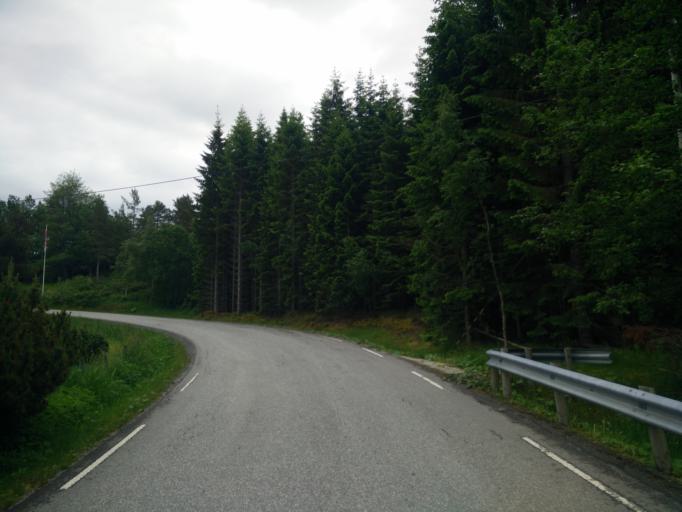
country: NO
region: More og Romsdal
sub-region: Kristiansund
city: Rensvik
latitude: 63.0156
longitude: 7.9644
